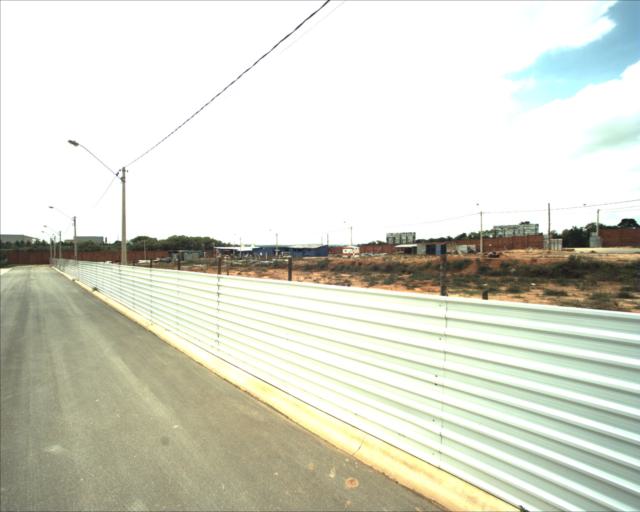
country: BR
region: Sao Paulo
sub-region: Sorocaba
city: Sorocaba
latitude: -23.4497
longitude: -47.3877
